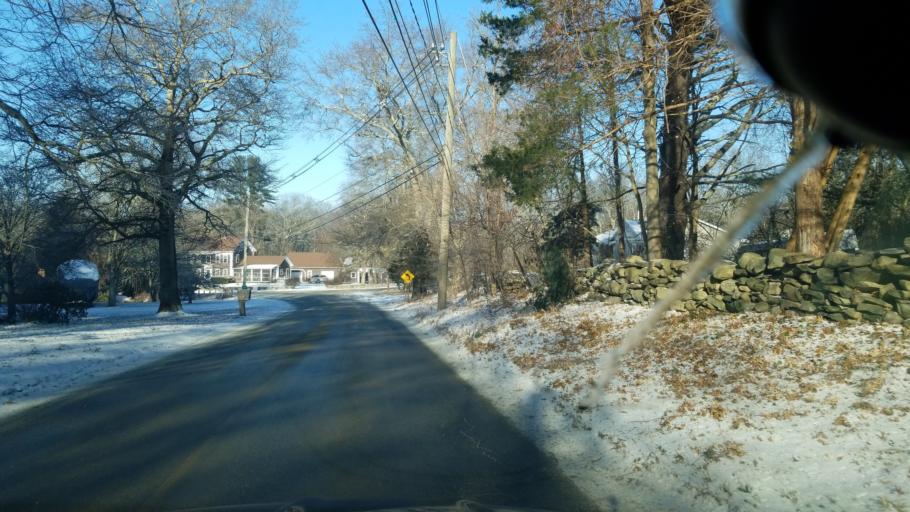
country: US
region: Connecticut
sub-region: Windham County
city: East Brooklyn
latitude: 41.8122
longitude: -71.9078
